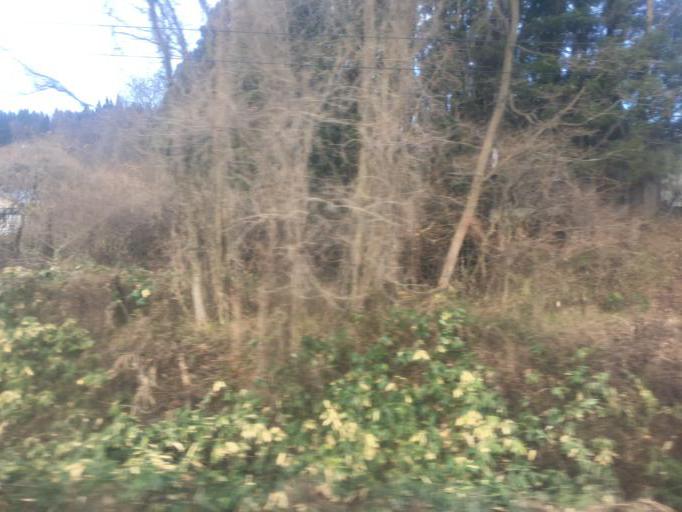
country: JP
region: Akita
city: Takanosu
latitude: 40.2639
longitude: 140.4328
